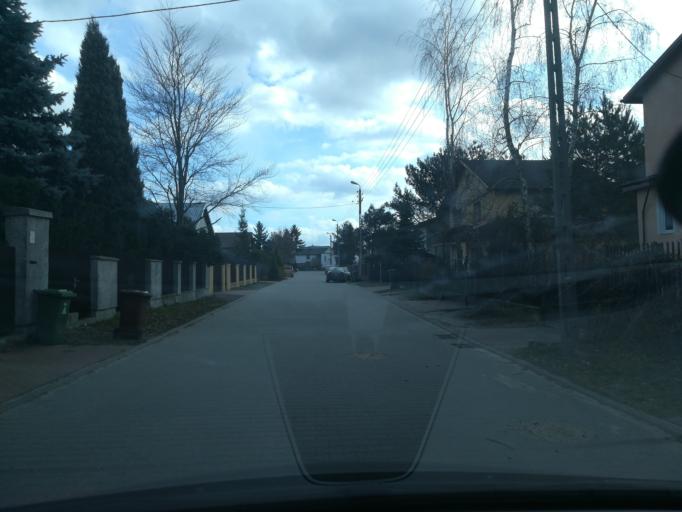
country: PL
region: Kujawsko-Pomorskie
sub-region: Powiat torunski
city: Lubicz Dolny
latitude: 52.9759
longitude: 18.6828
